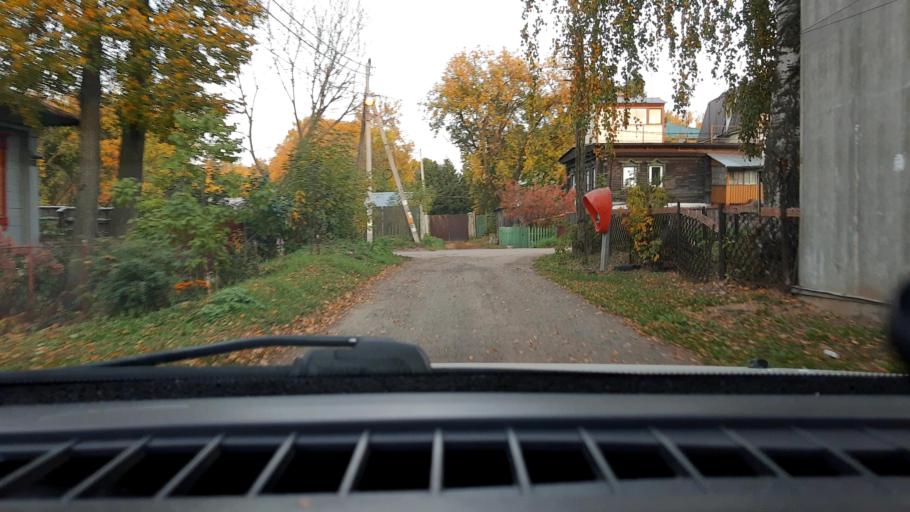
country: RU
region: Nizjnij Novgorod
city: Neklyudovo
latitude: 56.3643
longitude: 43.8552
